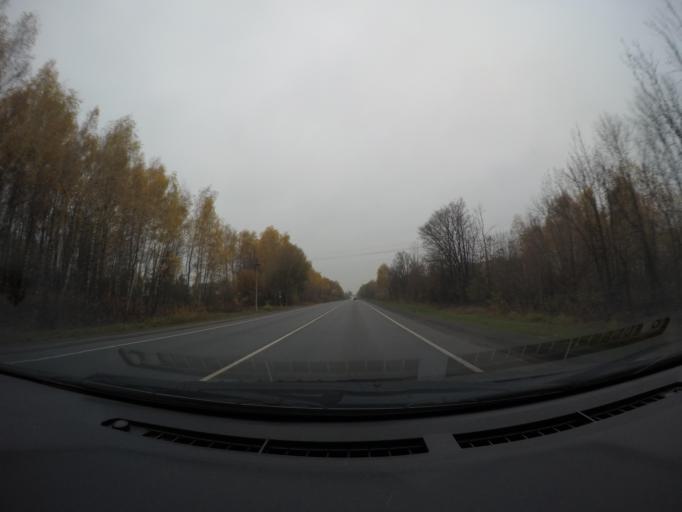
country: RU
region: Moskovskaya
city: Yakovlevskoye
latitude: 55.3673
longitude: 38.0632
